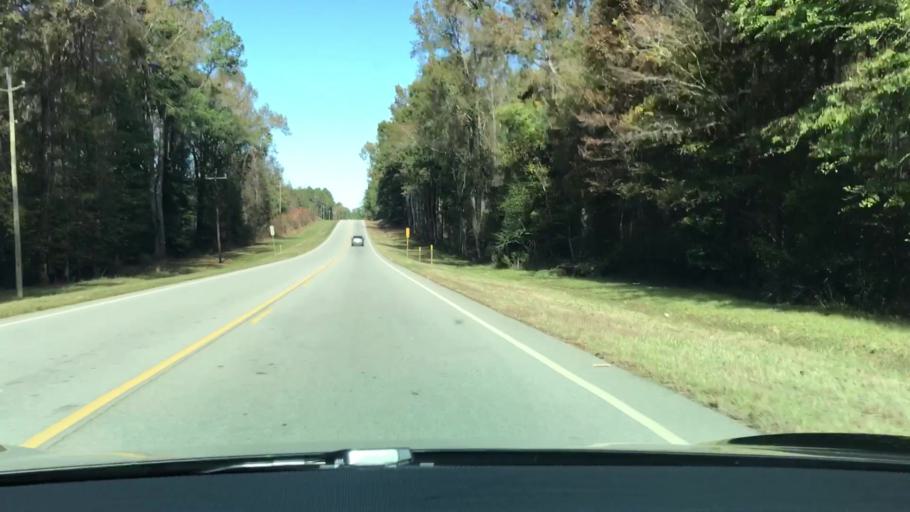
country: US
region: Georgia
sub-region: Warren County
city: Firing Range
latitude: 33.4314
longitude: -82.6863
